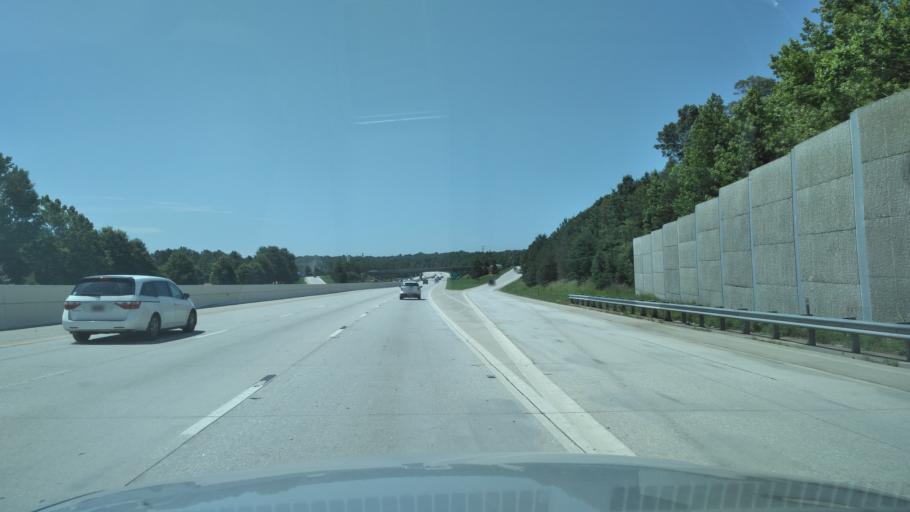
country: US
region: South Carolina
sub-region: Greenville County
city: Mauldin
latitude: 34.7949
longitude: -82.2802
